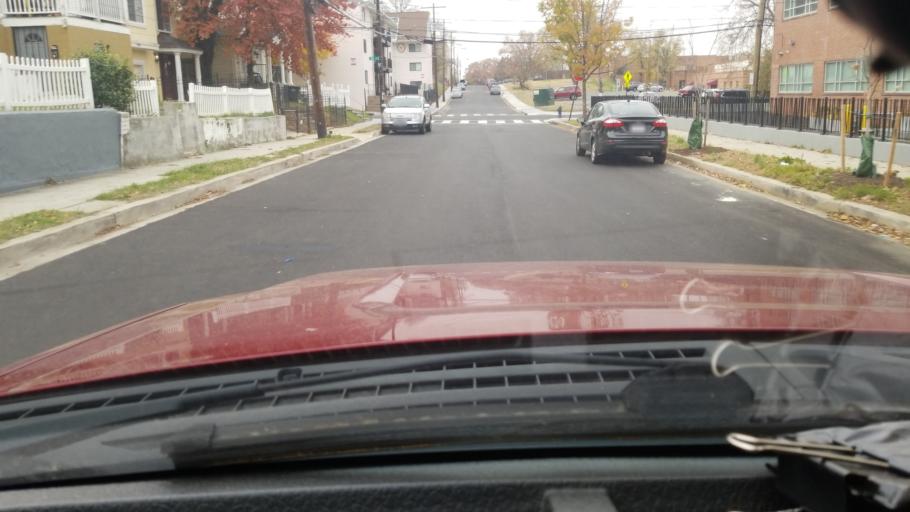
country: US
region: Maryland
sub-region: Prince George's County
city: Capitol Heights
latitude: 38.8886
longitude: -76.9293
